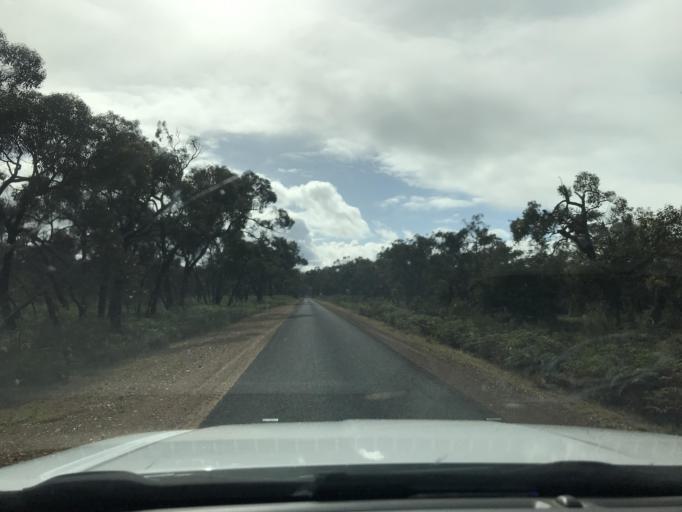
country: AU
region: South Australia
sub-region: Wattle Range
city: Penola
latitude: -37.1893
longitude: 141.2468
